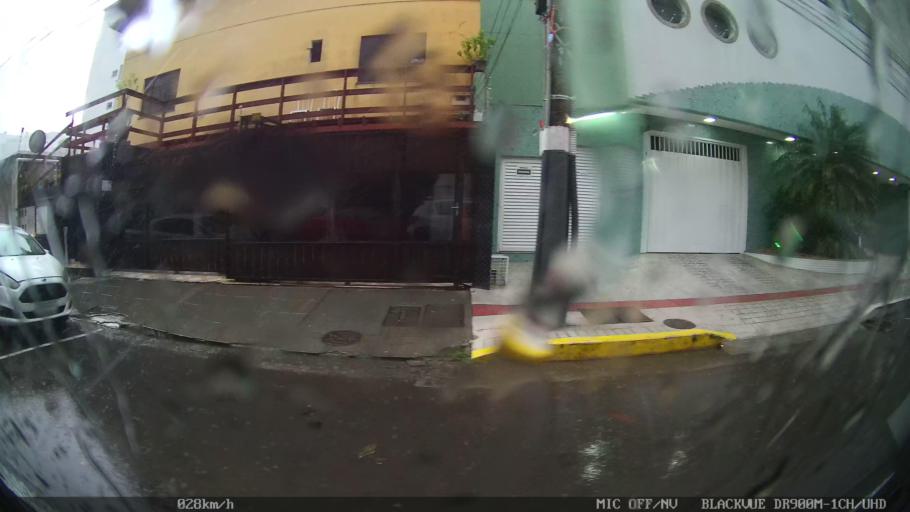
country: BR
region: Santa Catarina
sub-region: Balneario Camboriu
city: Balneario Camboriu
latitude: -26.9715
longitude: -48.6371
